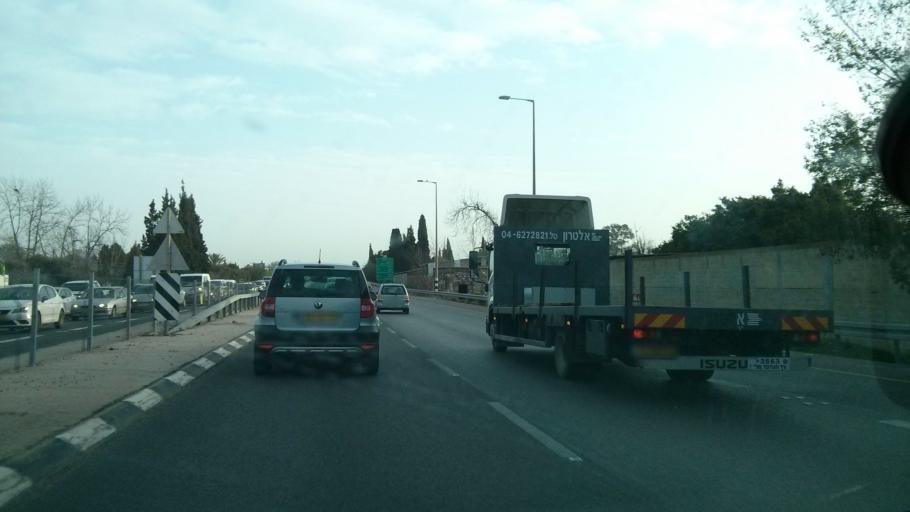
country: PS
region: West Bank
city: Nazlat `Isa
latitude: 32.4657
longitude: 34.9948
